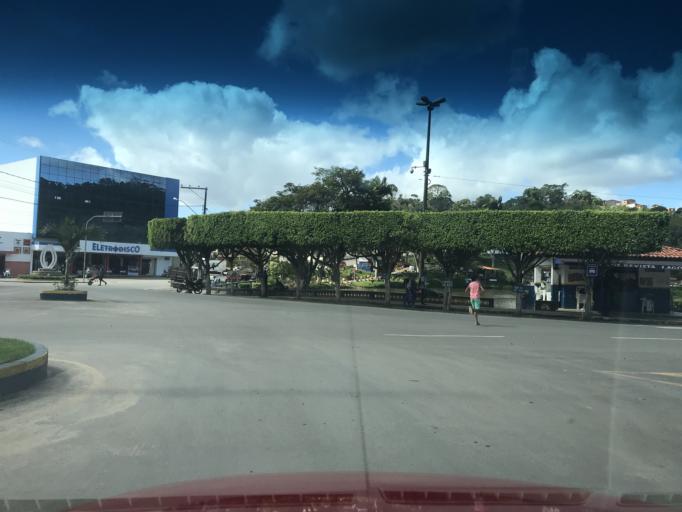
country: BR
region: Bahia
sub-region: Gandu
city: Gandu
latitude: -13.7451
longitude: -39.4856
